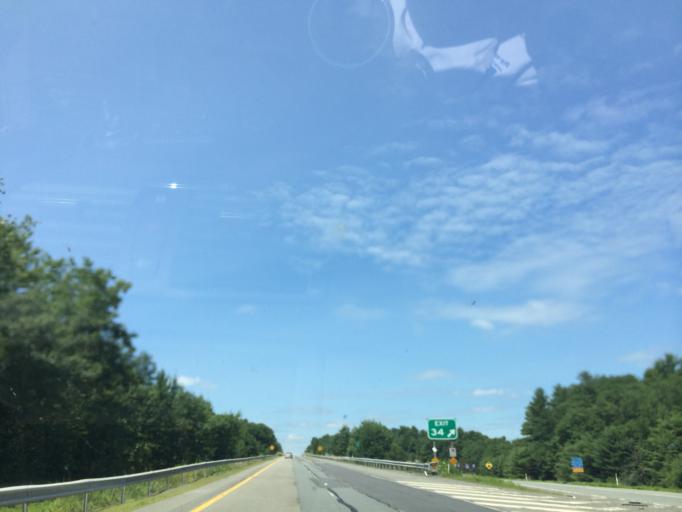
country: US
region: Pennsylvania
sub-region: Pike County
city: Hemlock Farms
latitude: 41.3583
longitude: -75.0513
